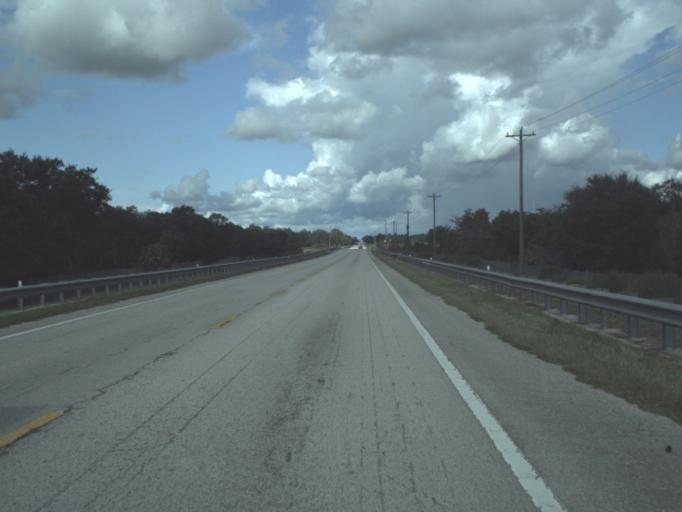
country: US
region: Florida
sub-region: DeSoto County
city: Arcadia
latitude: 27.2556
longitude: -81.9686
